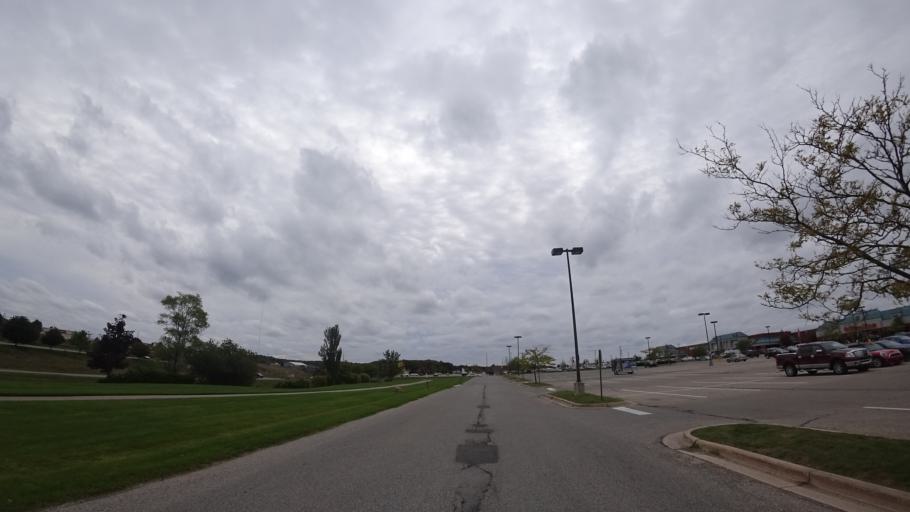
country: US
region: Michigan
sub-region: Emmet County
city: Petoskey
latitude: 45.3521
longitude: -84.9717
